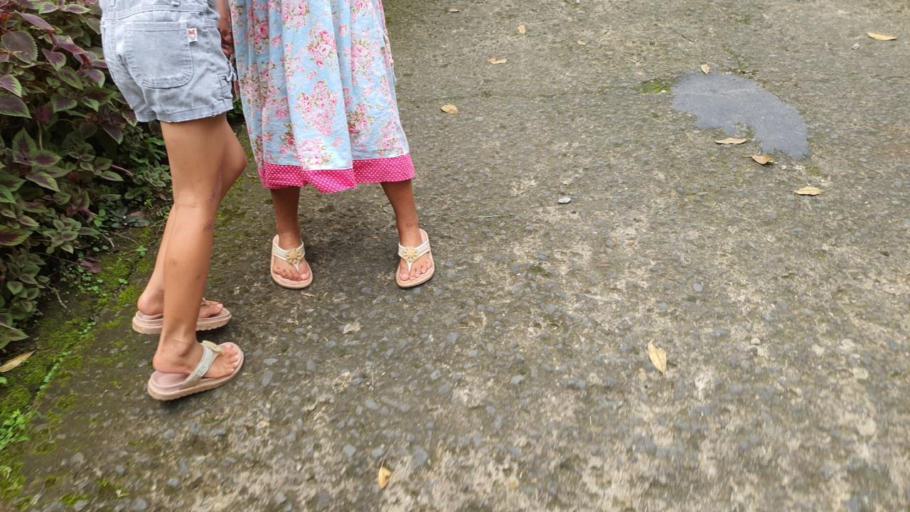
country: ID
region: West Java
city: Caringin
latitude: -6.6509
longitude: 106.8809
